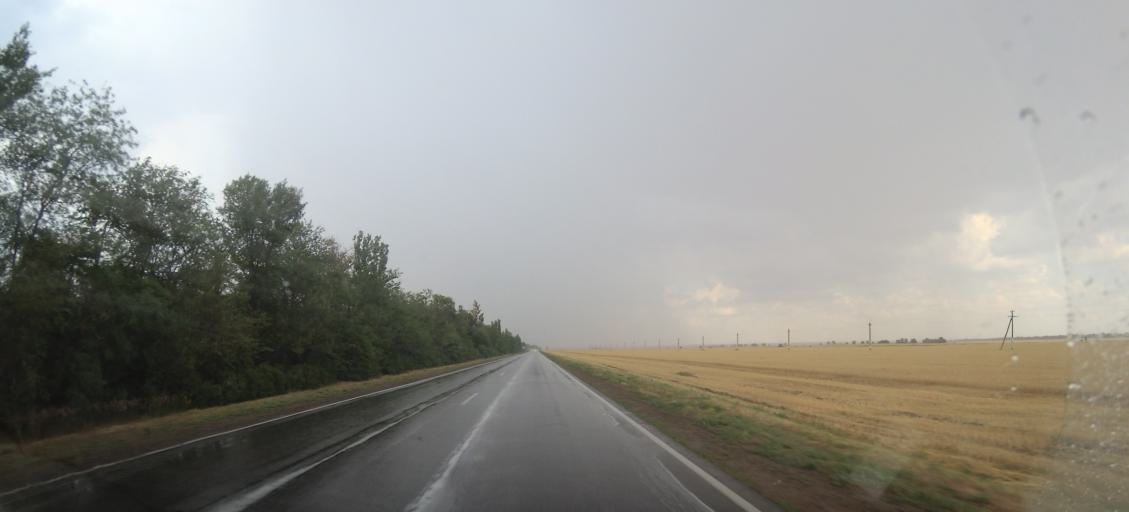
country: RU
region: Rostov
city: Proletarsk
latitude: 46.6621
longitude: 41.6864
